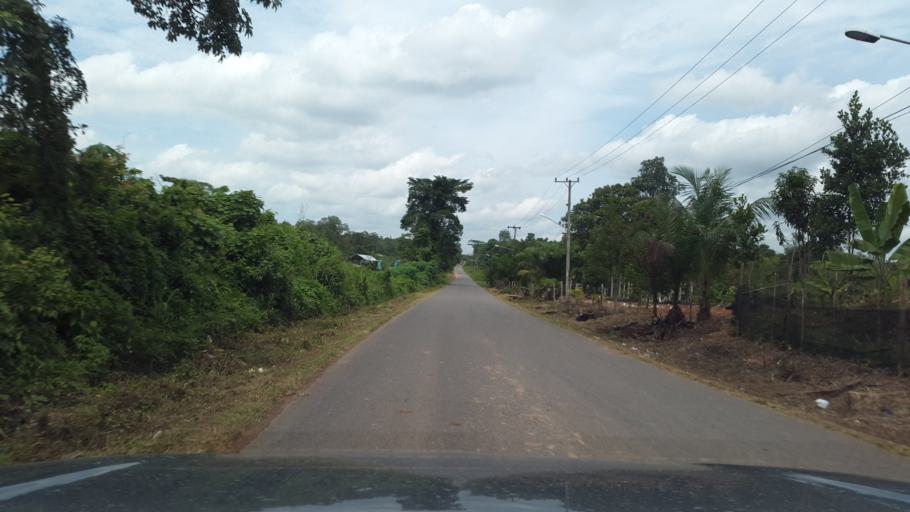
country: ID
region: South Sumatra
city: Gunungmegang Dalam
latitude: -3.3489
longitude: 103.9186
